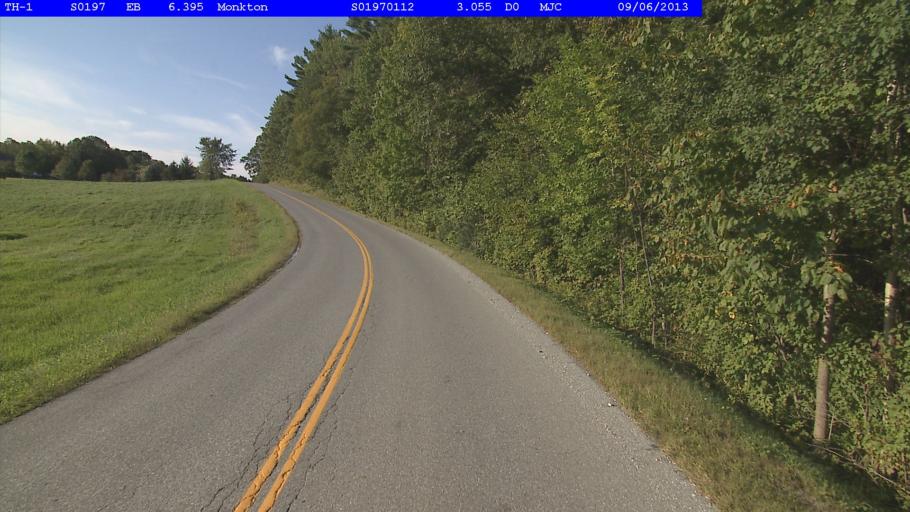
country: US
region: Vermont
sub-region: Addison County
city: Bristol
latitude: 44.2214
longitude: -73.1524
